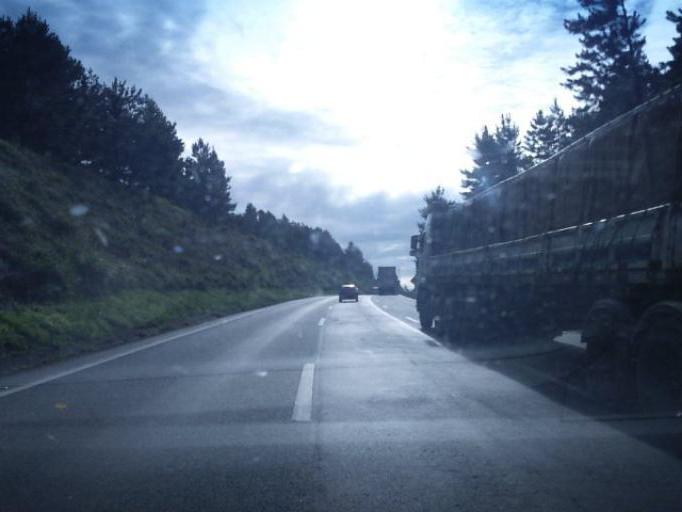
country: BR
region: Parana
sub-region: Campina Grande Do Sul
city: Campina Grande do Sul
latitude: -25.1046
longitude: -48.8380
